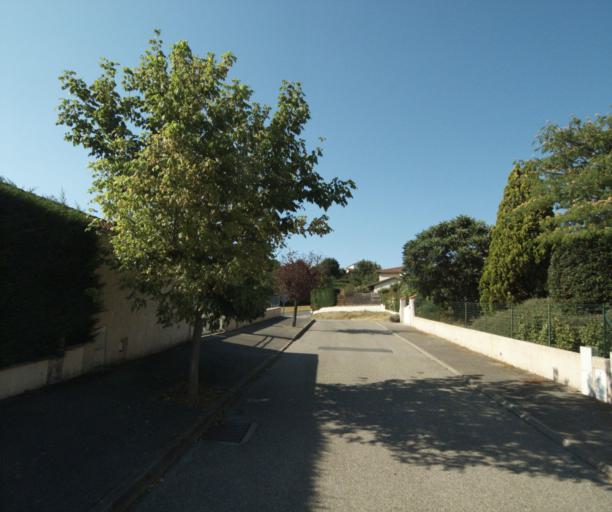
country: FR
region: Rhone-Alpes
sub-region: Departement du Rhone
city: Saint-Pierre-la-Palud
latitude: 45.7874
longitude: 4.6108
